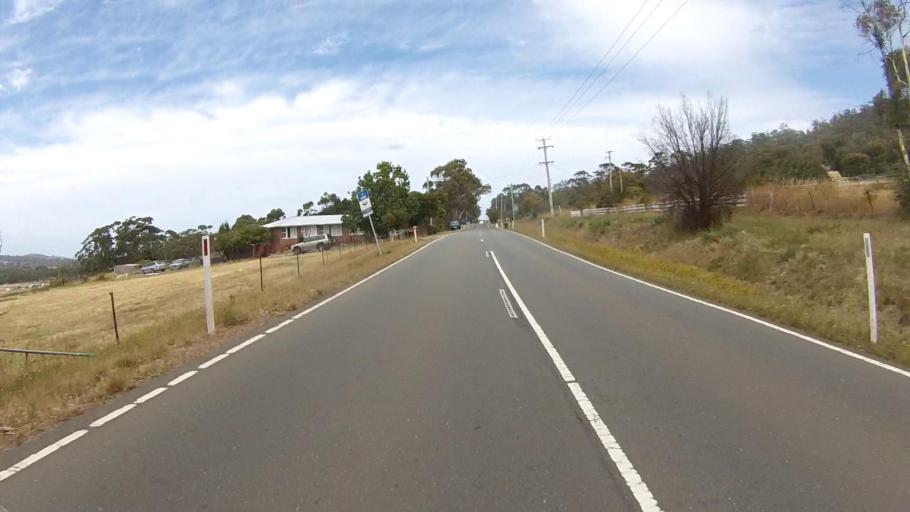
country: AU
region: Tasmania
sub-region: Clarence
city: Acton Park
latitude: -42.8939
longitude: 147.4817
